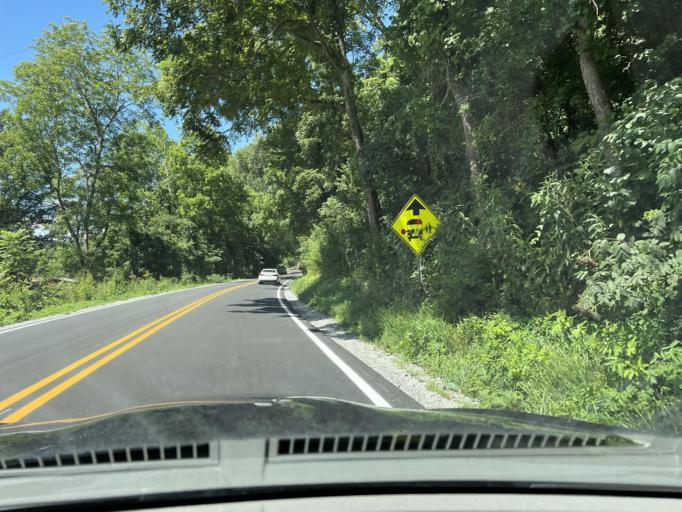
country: US
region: North Carolina
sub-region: Buncombe County
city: Fairview
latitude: 35.5157
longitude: -82.4066
